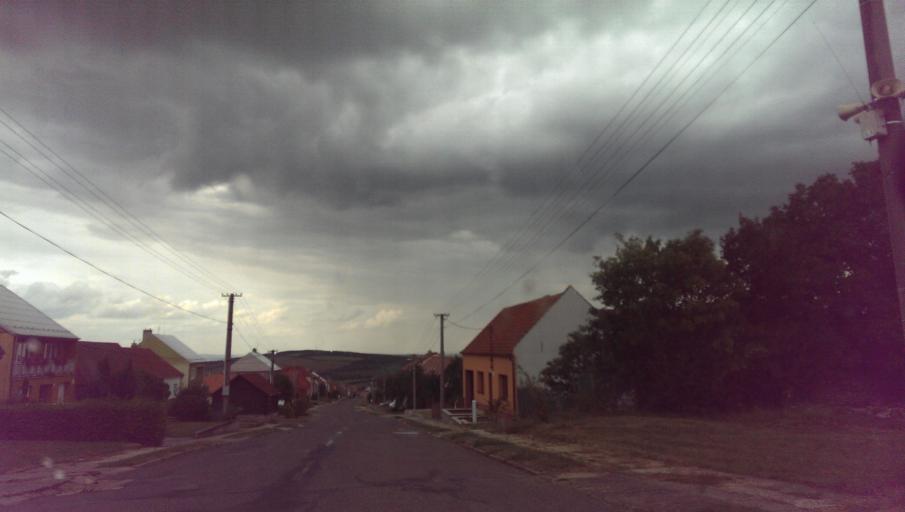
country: CZ
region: South Moravian
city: Velka nad Velickou
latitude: 48.9043
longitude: 17.5642
